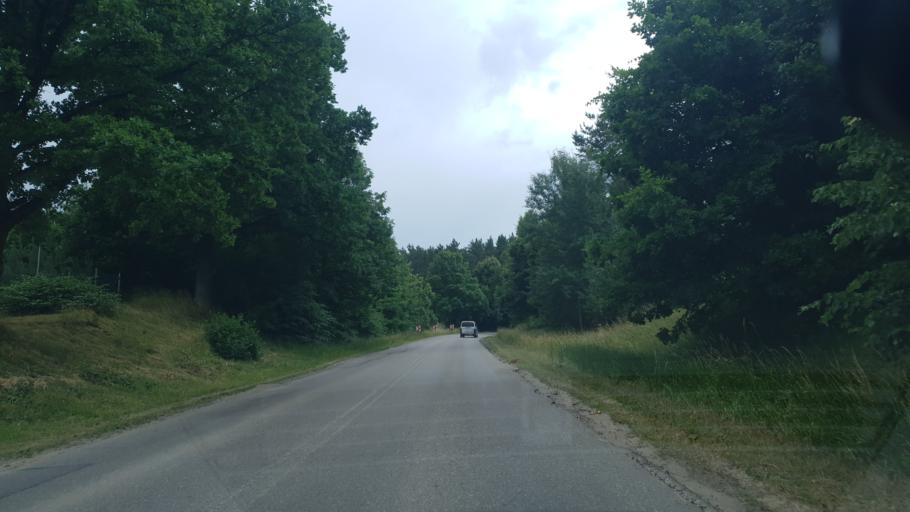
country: PL
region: Pomeranian Voivodeship
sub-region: Powiat kartuski
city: Przodkowo
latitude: 54.3656
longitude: 18.2658
